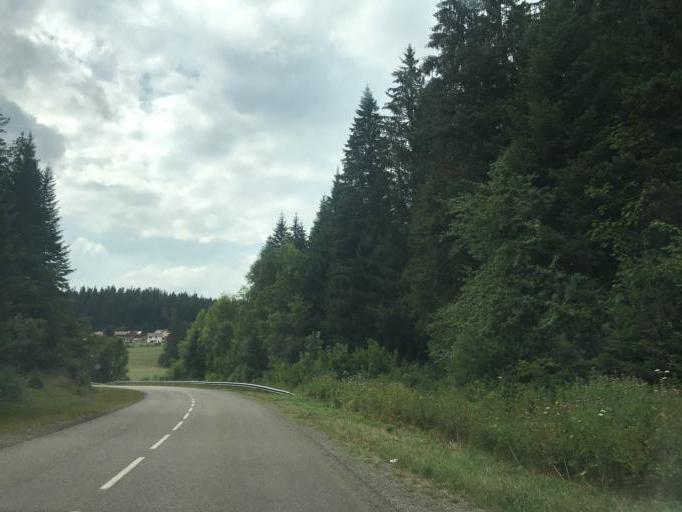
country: FR
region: Franche-Comte
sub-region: Departement du Jura
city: Longchaumois
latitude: 46.5010
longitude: 5.9109
